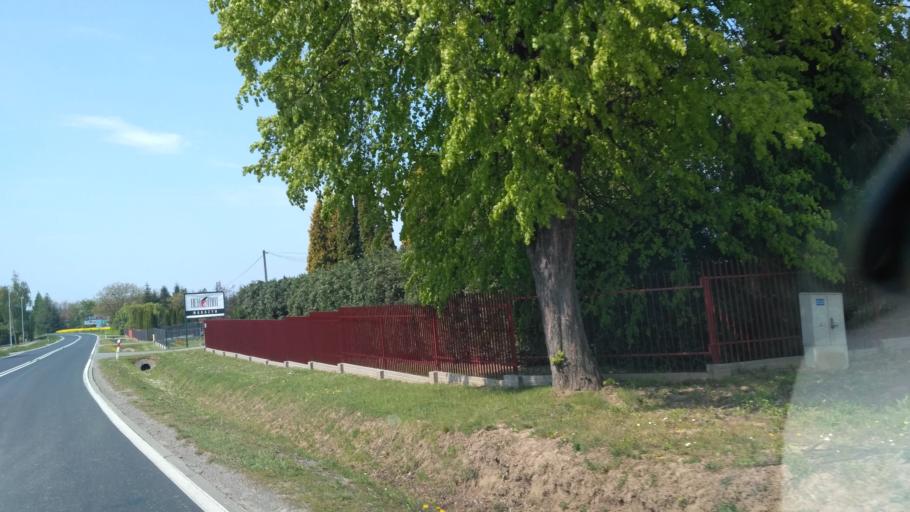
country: PL
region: Subcarpathian Voivodeship
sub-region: Powiat jaroslawski
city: Pawlosiow
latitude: 49.9833
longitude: 22.6507
